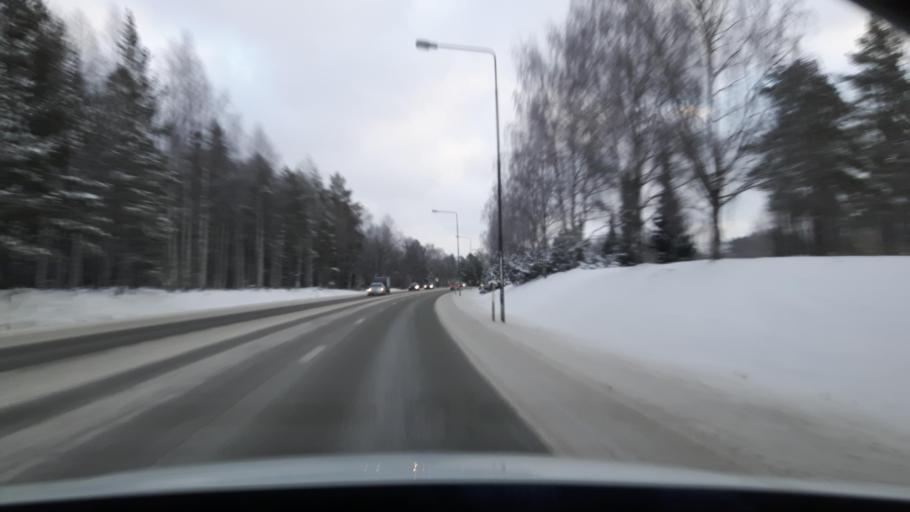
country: SE
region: Vaesterbotten
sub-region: Umea Kommun
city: Umea
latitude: 63.8478
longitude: 20.2865
